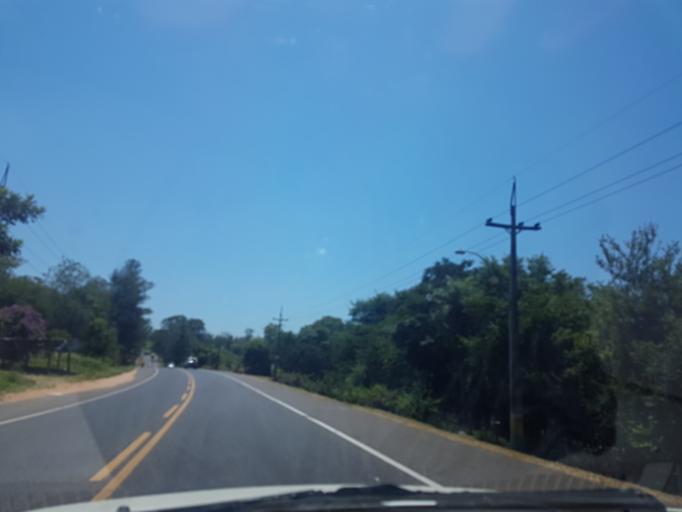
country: PY
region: Cordillera
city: Caacupe
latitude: -25.3908
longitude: -57.0703
